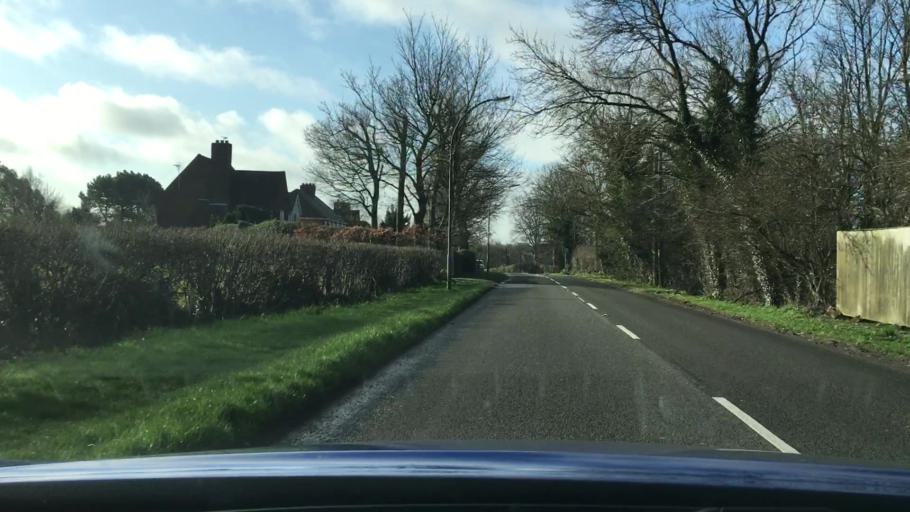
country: GB
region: England
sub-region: Derbyshire
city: Tibshelf
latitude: 53.1533
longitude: -1.3376
